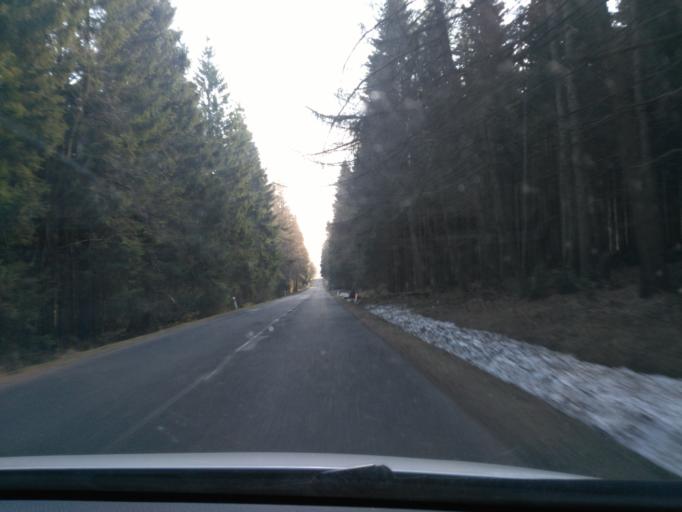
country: CZ
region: Ustecky
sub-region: Okres Chomutov
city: Vejprty
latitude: 50.4883
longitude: 13.0477
